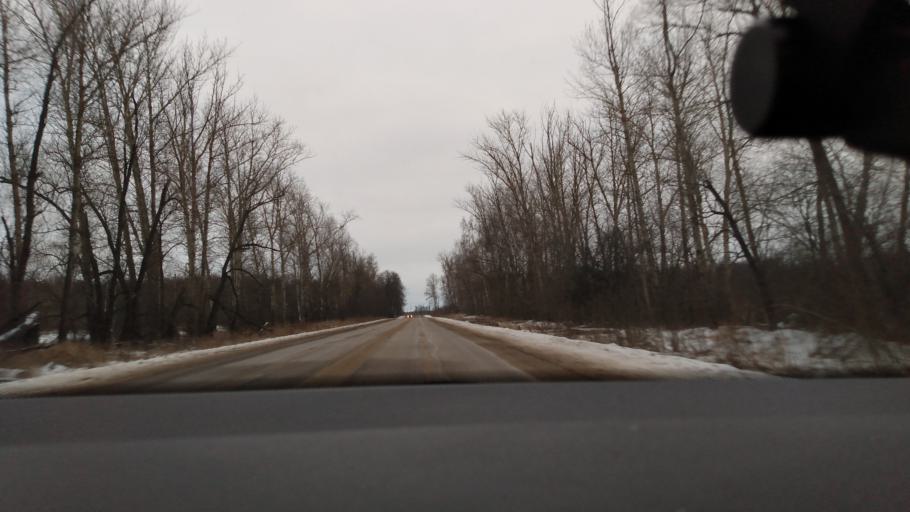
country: RU
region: Moskovskaya
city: Krasnaya Poyma
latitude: 55.1185
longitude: 39.1491
